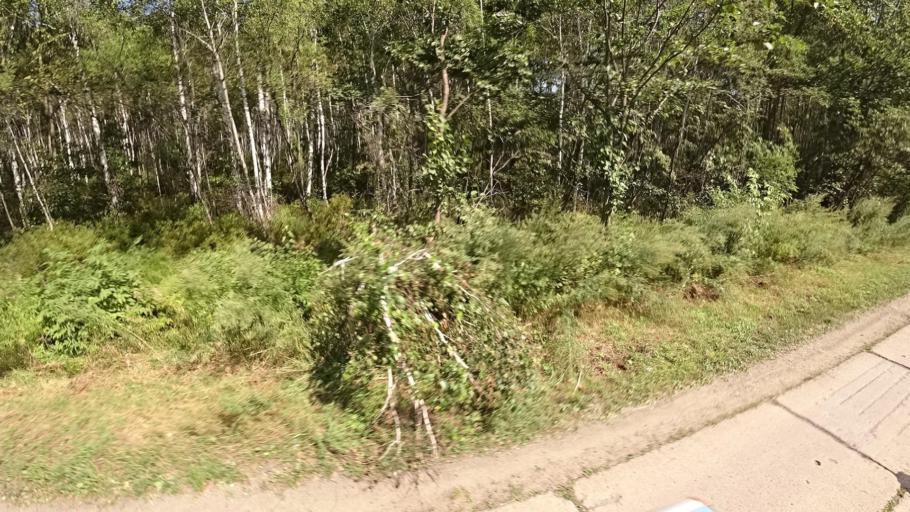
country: RU
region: Khabarovsk Krai
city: Khor
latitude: 47.9900
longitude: 135.0946
